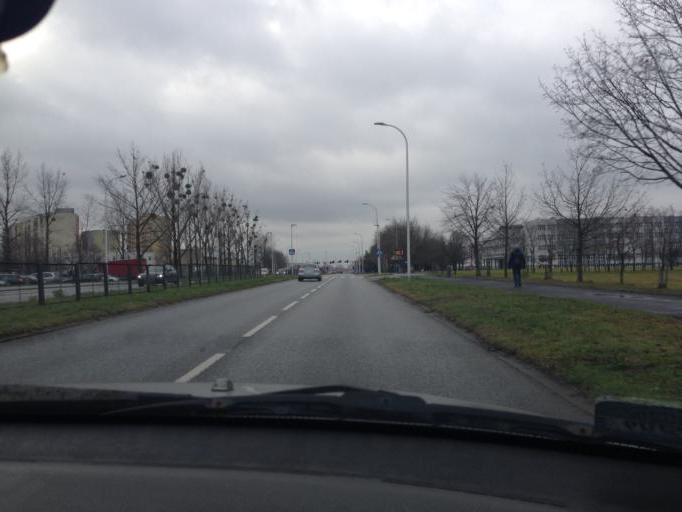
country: PL
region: Opole Voivodeship
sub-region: Powiat opolski
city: Opole
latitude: 50.6849
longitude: 17.9482
